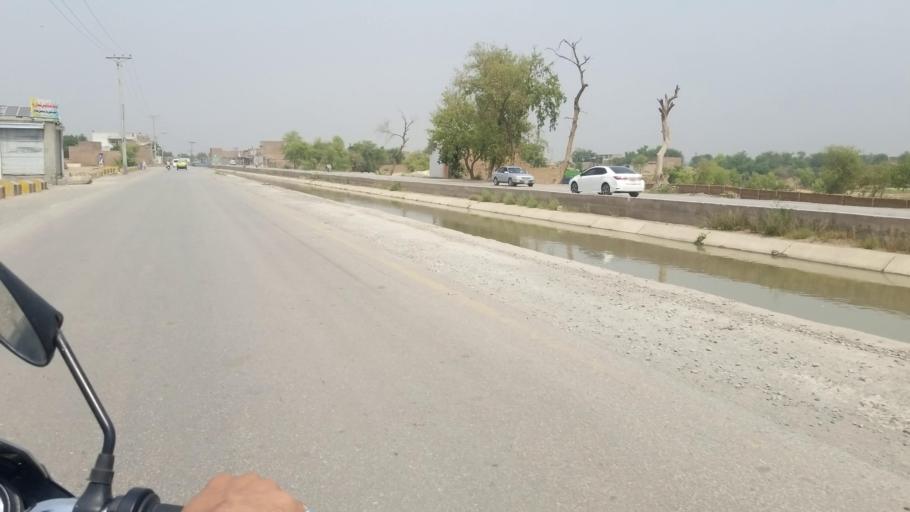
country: PK
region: Khyber Pakhtunkhwa
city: Peshawar
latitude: 33.9536
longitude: 71.5514
